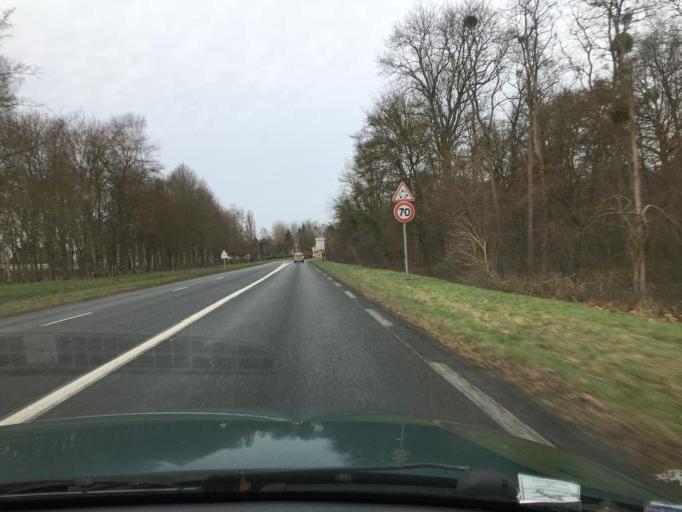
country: FR
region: Picardie
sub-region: Departement de l'Oise
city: Senlis
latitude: 49.1893
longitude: 2.5727
